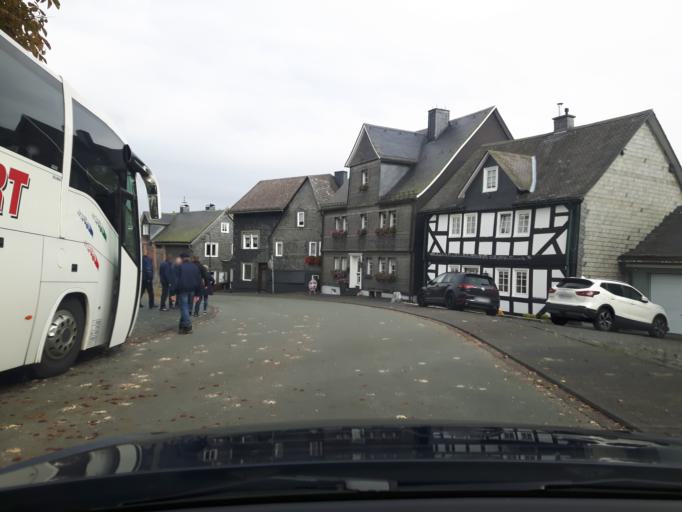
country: DE
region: North Rhine-Westphalia
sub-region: Regierungsbezirk Arnsberg
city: Bad Berleburg
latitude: 51.0511
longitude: 8.3894
